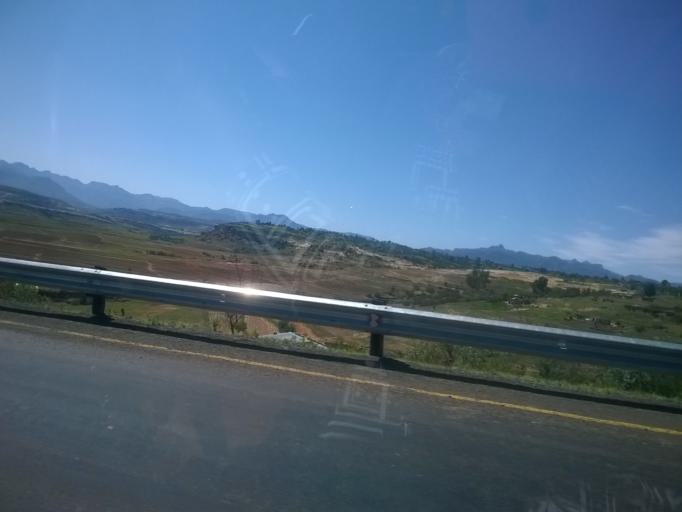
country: LS
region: Leribe
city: Maputsoe
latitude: -29.0959
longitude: 27.9613
